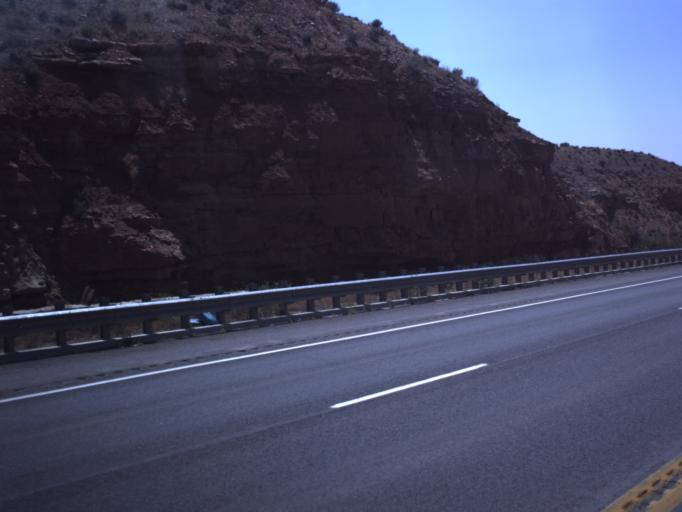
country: US
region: Utah
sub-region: Uintah County
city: Maeser
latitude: 40.3478
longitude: -109.6255
